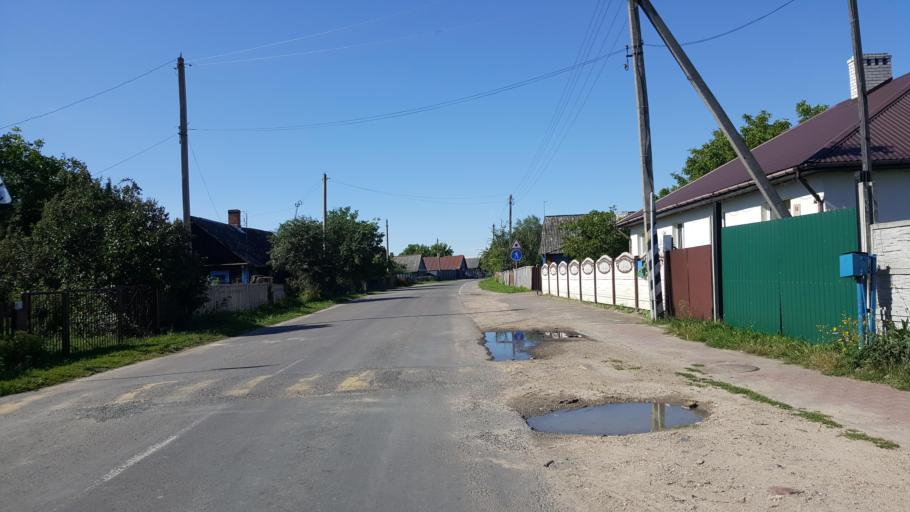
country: BY
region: Brest
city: Charnawchytsy
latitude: 52.2216
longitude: 23.7390
